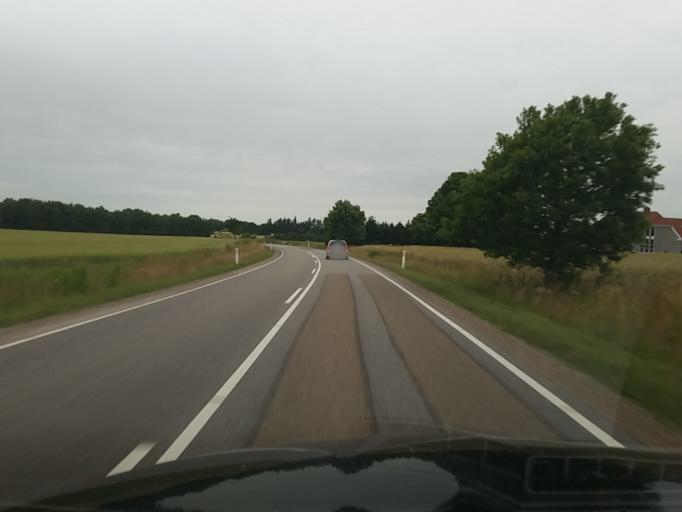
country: DK
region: South Denmark
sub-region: Billund Kommune
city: Grindsted
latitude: 55.6611
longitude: 8.7764
